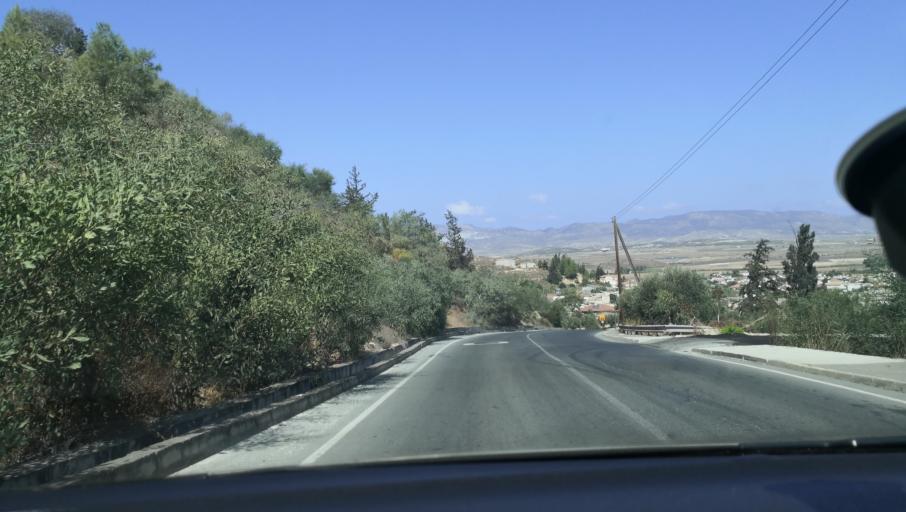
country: CY
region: Lefkosia
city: Mammari
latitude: 35.1704
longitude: 33.2018
